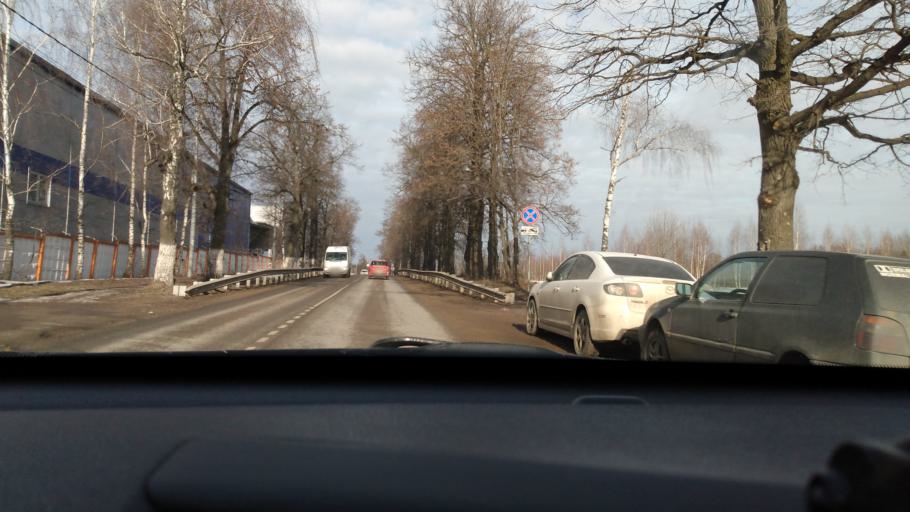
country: RU
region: Moskovskaya
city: Nakhabino
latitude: 55.8612
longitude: 37.1862
